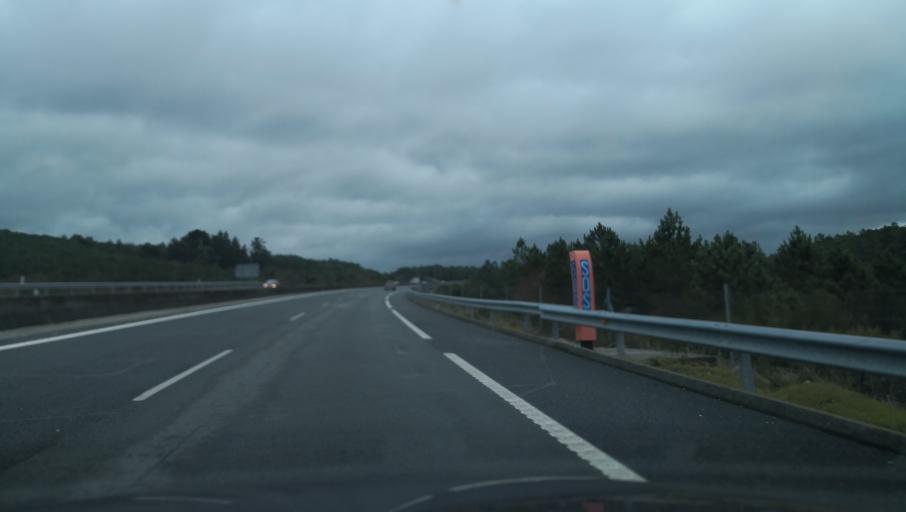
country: ES
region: Galicia
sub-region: Provincia de Ourense
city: Pinor
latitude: 42.5292
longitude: -8.0158
